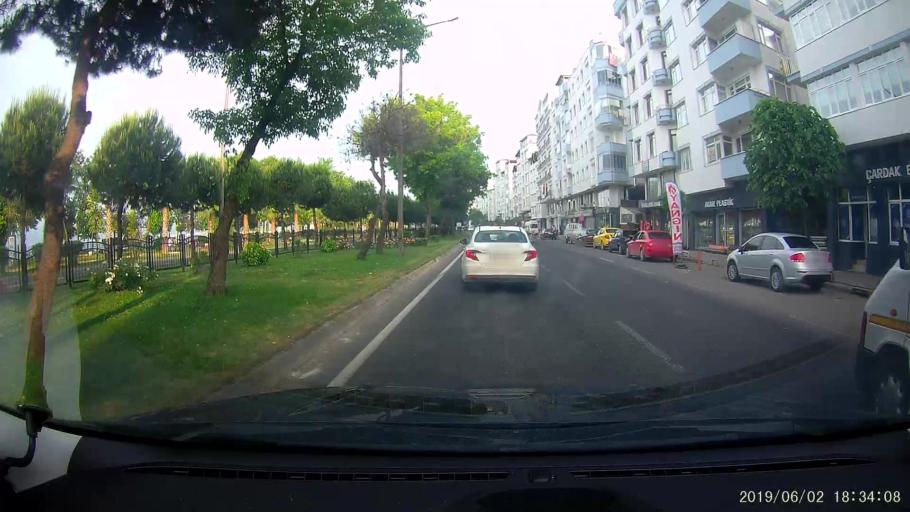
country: TR
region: Ordu
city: Fatsa
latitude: 41.0310
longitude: 37.5013
